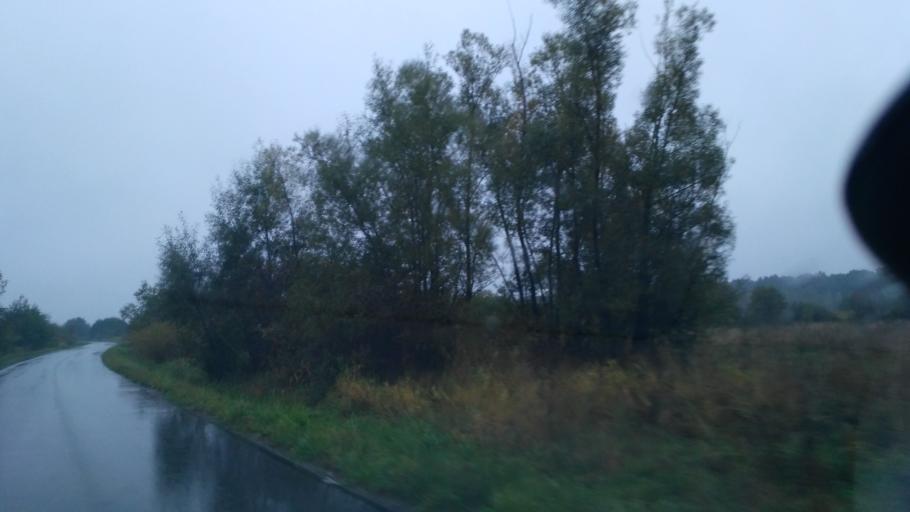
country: PL
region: Subcarpathian Voivodeship
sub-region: Powiat krosnienski
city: Kroscienko Wyzne
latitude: 49.6622
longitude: 21.8035
